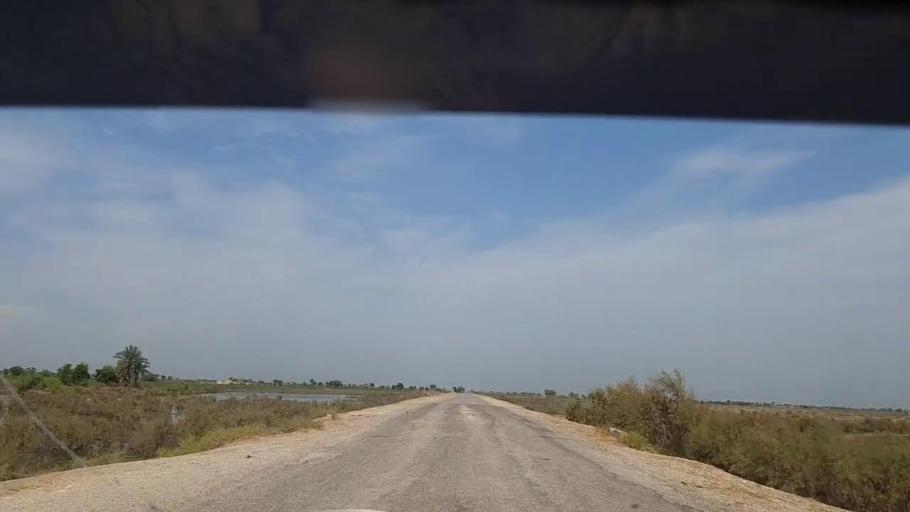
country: PK
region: Sindh
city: Thul
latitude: 28.1905
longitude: 68.7639
